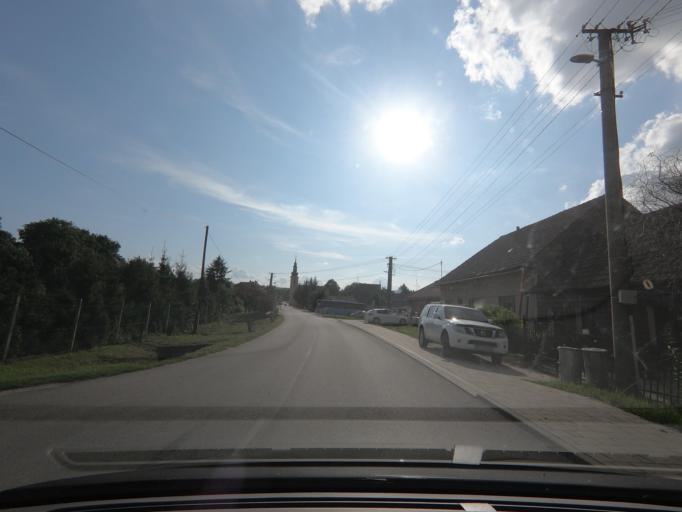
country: SK
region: Nitriansky
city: Stara Tura
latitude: 48.7373
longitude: 17.7107
